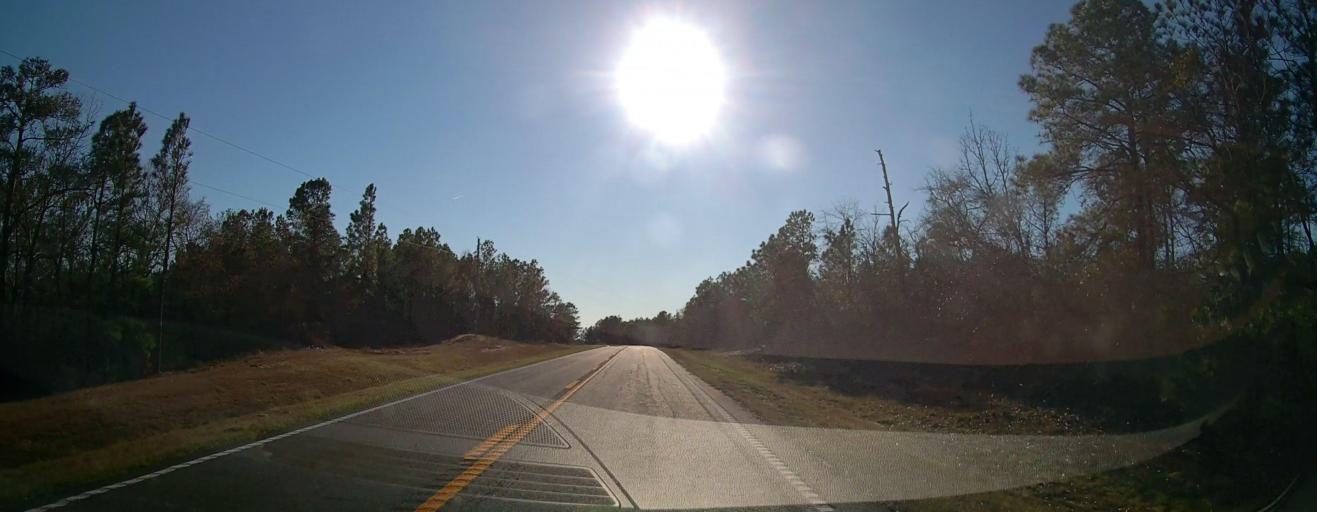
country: US
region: Georgia
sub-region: Taylor County
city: Butler
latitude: 32.5506
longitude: -84.2746
